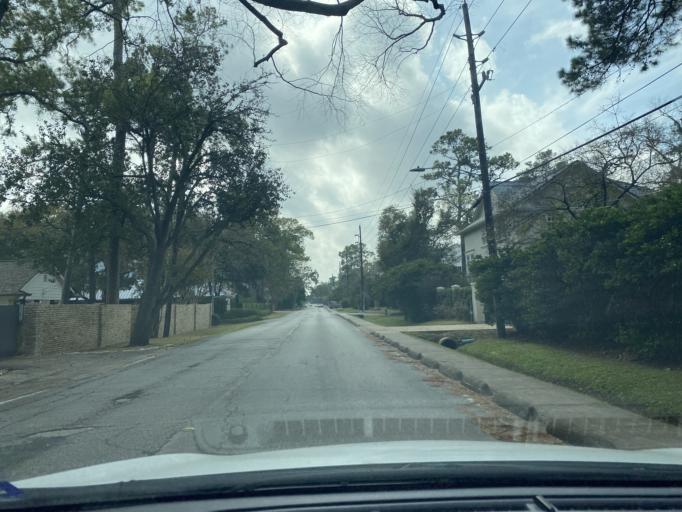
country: US
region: Texas
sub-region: Harris County
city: Hunters Creek Village
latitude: 29.7660
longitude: -95.4677
